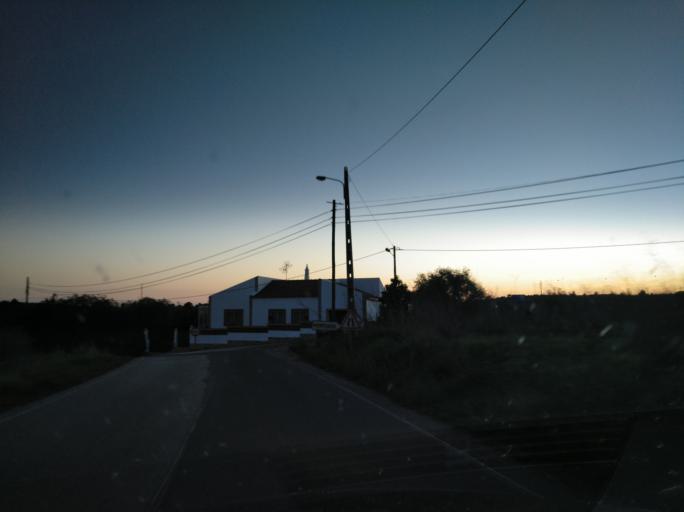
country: PT
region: Faro
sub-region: Vila Real de Santo Antonio
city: Monte Gordo
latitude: 37.2012
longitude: -7.5133
